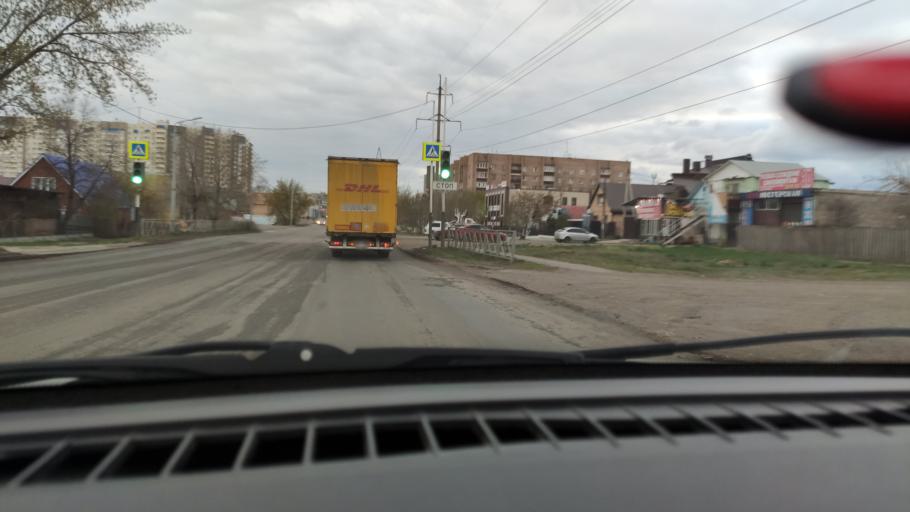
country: RU
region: Orenburg
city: Orenburg
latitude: 51.7858
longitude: 55.1764
